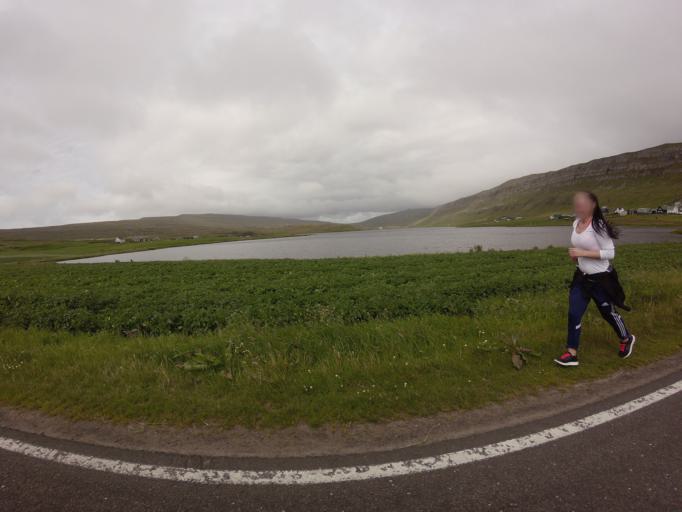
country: FO
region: Sandoy
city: Sandur
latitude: 61.8393
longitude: -6.8129
